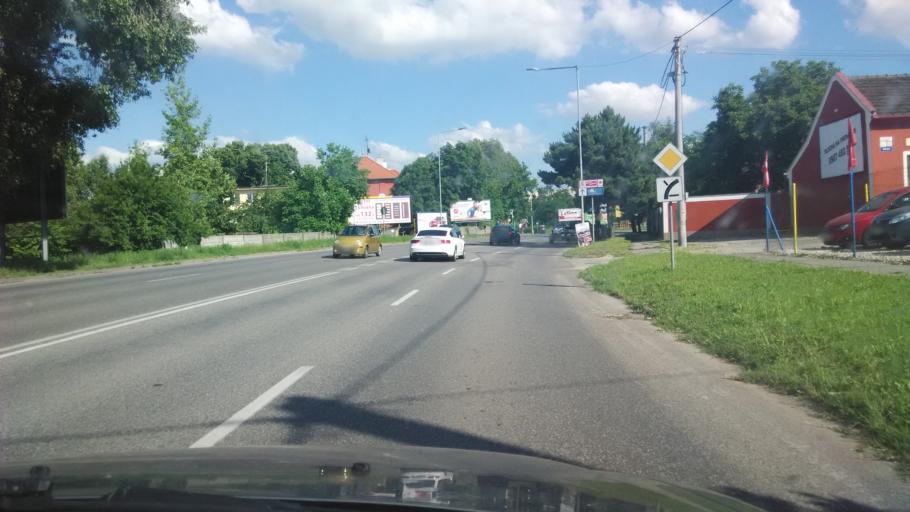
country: SK
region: Nitriansky
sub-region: Okres Nove Zamky
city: Nove Zamky
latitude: 47.9990
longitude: 18.1647
